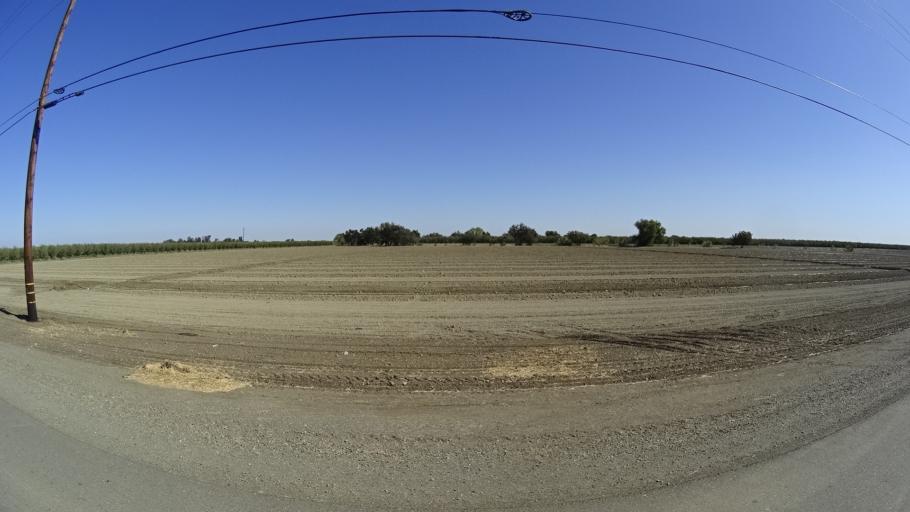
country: US
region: California
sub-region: Yolo County
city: Woodland
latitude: 38.6118
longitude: -121.8030
